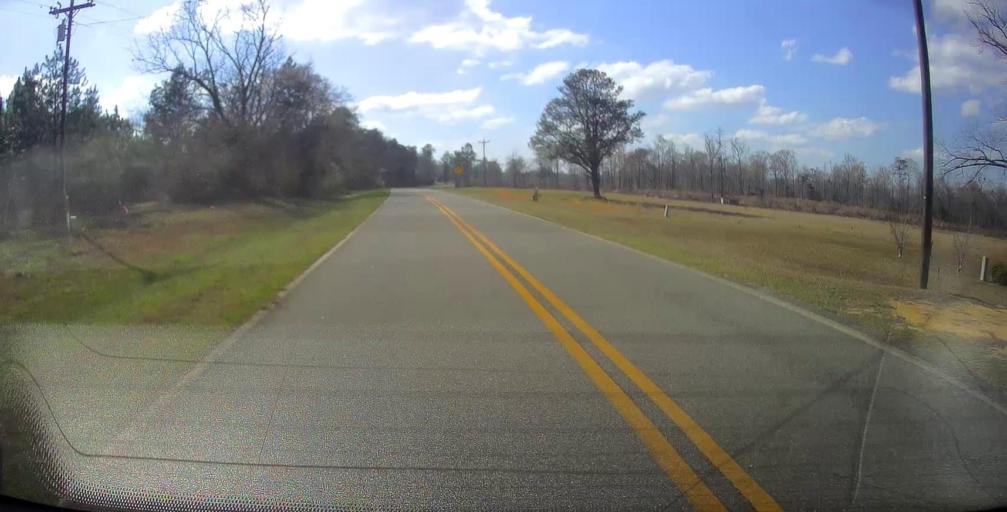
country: US
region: Georgia
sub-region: Wilkinson County
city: Irwinton
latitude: 32.6340
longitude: -83.1161
